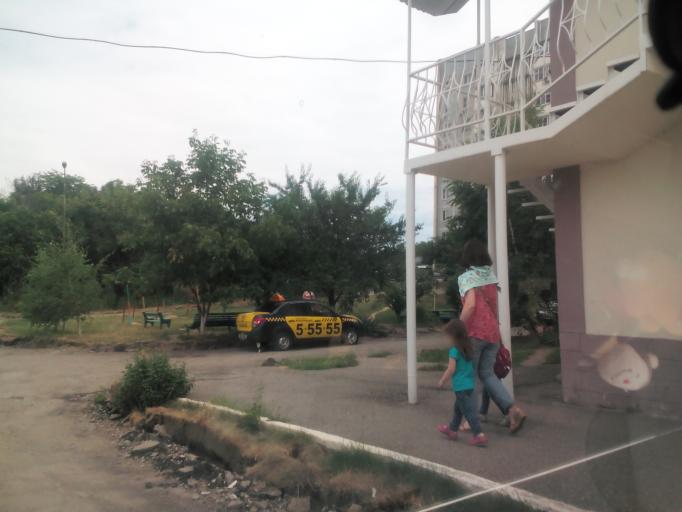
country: RU
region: Stavropol'skiy
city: Zheleznovodsk
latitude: 44.1507
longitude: 43.0026
